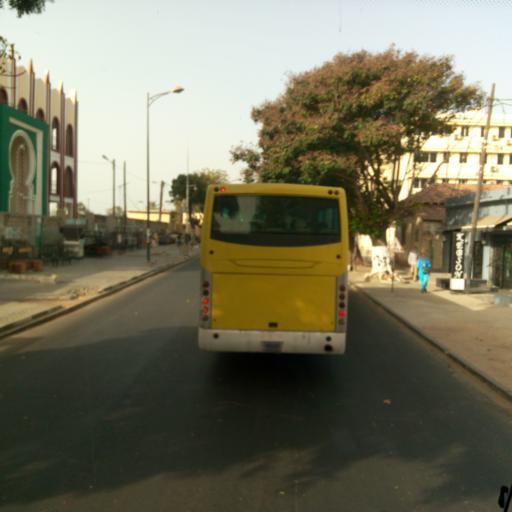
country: SN
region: Dakar
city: Dakar
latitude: 14.6746
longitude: -17.4488
